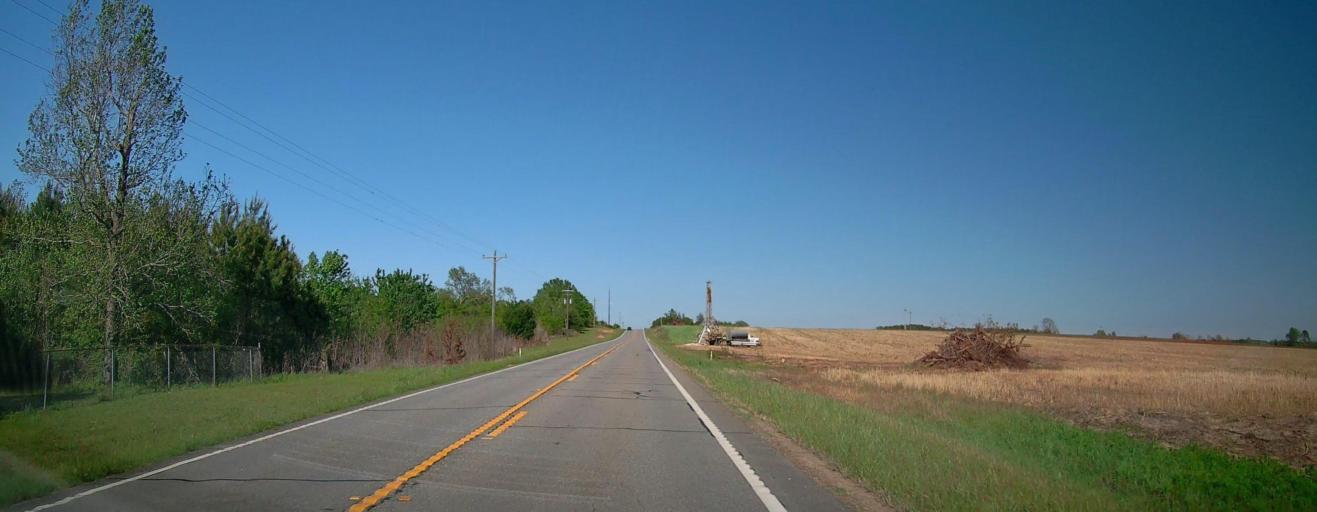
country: US
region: Georgia
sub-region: Pulaski County
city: Hawkinsville
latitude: 32.2469
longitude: -83.5866
